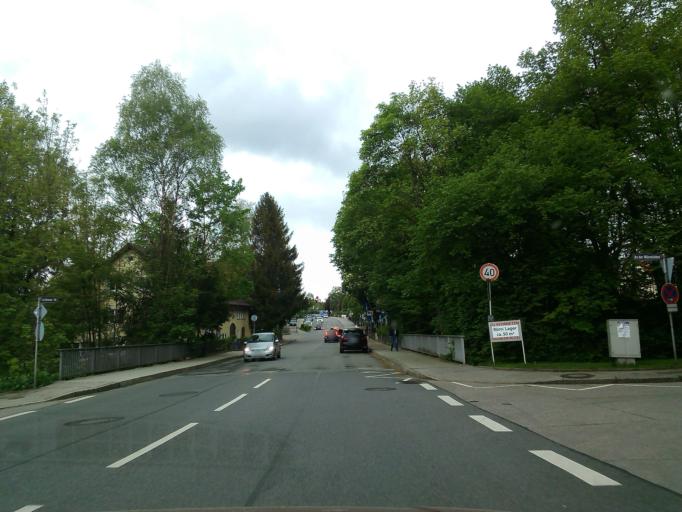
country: DE
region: Bavaria
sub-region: Upper Bavaria
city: Pasing
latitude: 48.1254
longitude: 11.4470
